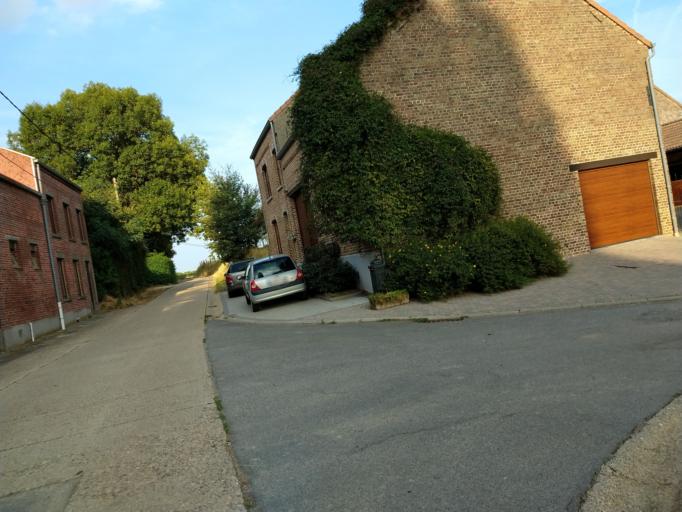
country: BE
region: Flanders
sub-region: Provincie Vlaams-Brabant
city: Boutersem
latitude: 50.8126
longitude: 4.8336
